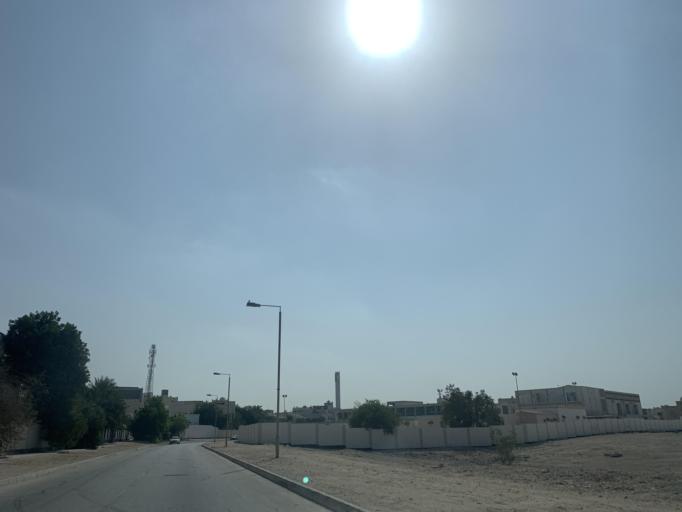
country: BH
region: Central Governorate
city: Madinat Hamad
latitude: 26.1287
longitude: 50.5034
